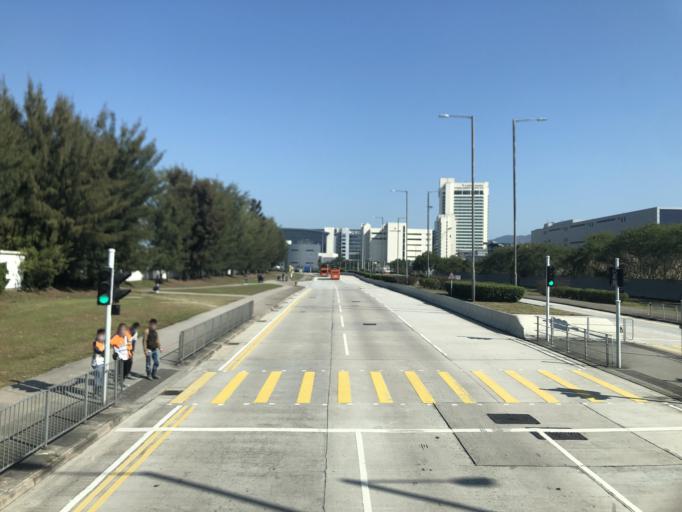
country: HK
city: Tai O
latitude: 22.2967
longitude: 113.9285
